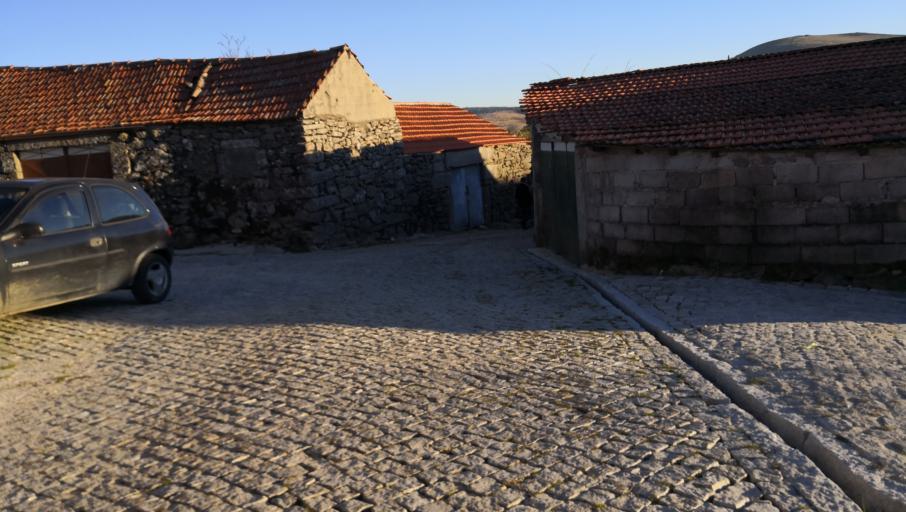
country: PT
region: Vila Real
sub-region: Ribeira de Pena
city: Ribeira de Pena
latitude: 41.5043
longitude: -7.7432
